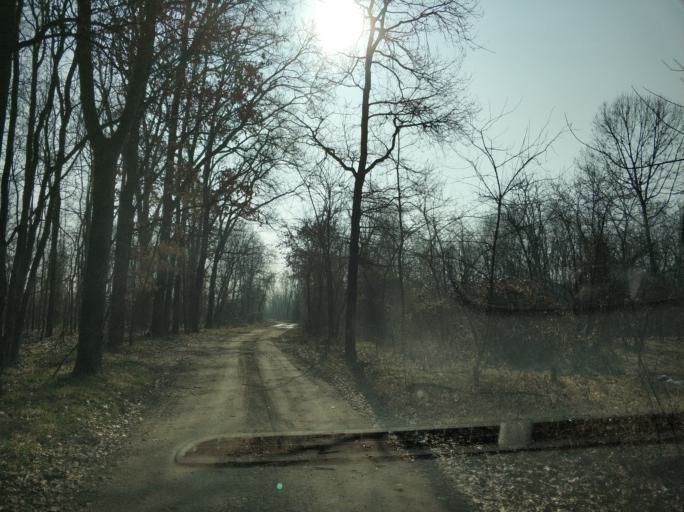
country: IT
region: Piedmont
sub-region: Provincia di Torino
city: Lombardore
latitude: 45.2444
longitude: 7.7375
